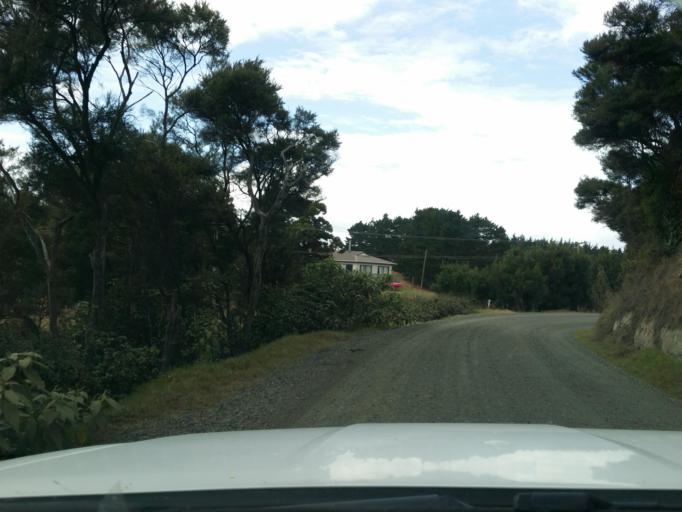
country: NZ
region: Auckland
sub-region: Auckland
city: Wellsford
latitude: -36.3146
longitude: 174.1337
